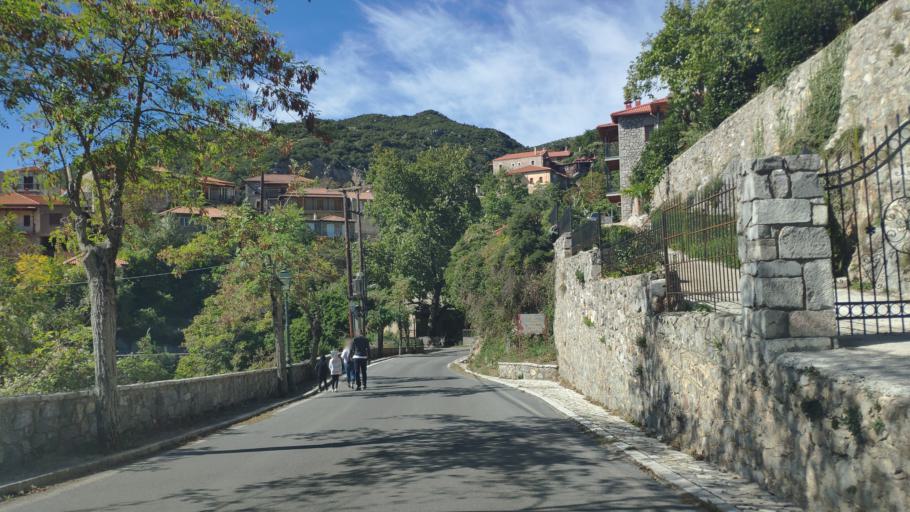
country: GR
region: Peloponnese
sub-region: Nomos Arkadias
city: Dimitsana
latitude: 37.5555
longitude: 22.0846
